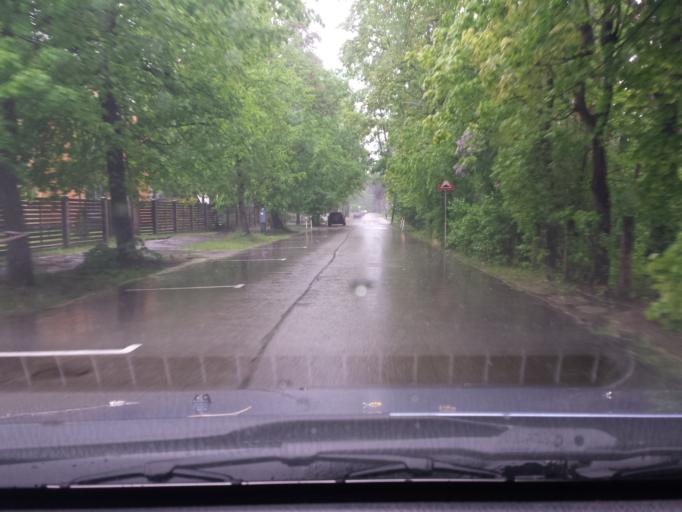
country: LV
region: Riga
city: Jaunciems
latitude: 57.0768
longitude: 24.1123
